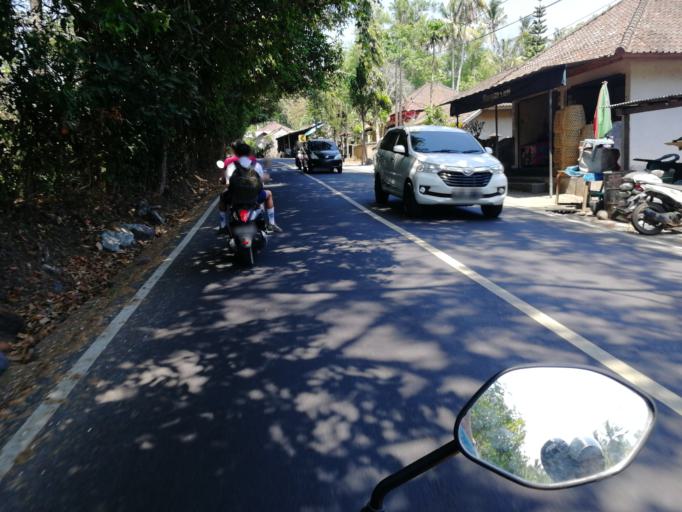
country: ID
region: Bali
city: Abang
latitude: -8.3907
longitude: 115.5988
